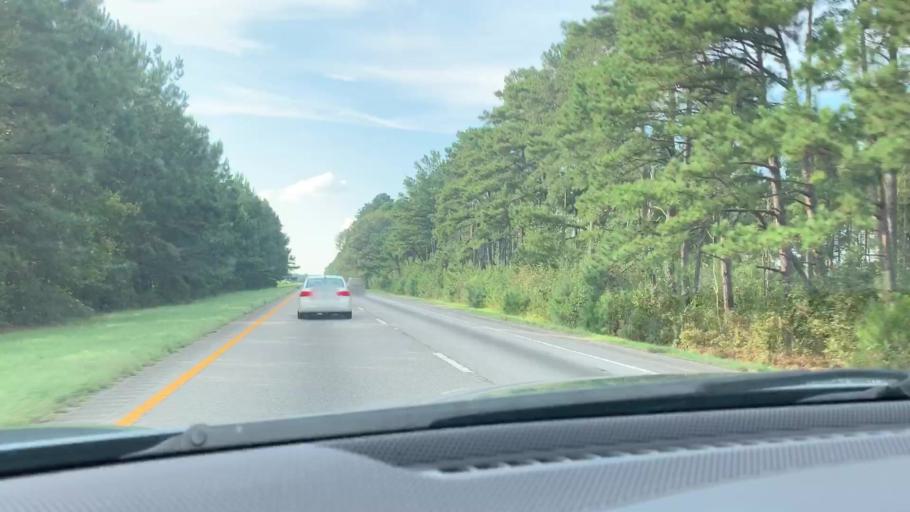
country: US
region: South Carolina
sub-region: Orangeburg County
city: Brookdale
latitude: 33.4378
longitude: -80.7023
